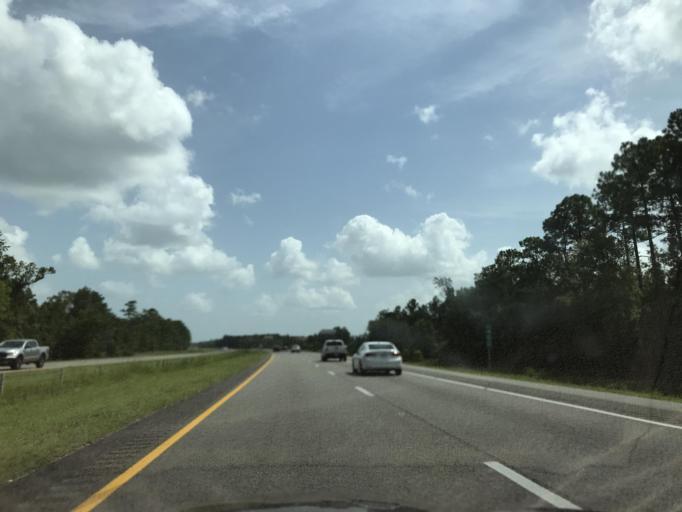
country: US
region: North Carolina
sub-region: Pender County
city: Burgaw
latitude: 34.5255
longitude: -77.8905
